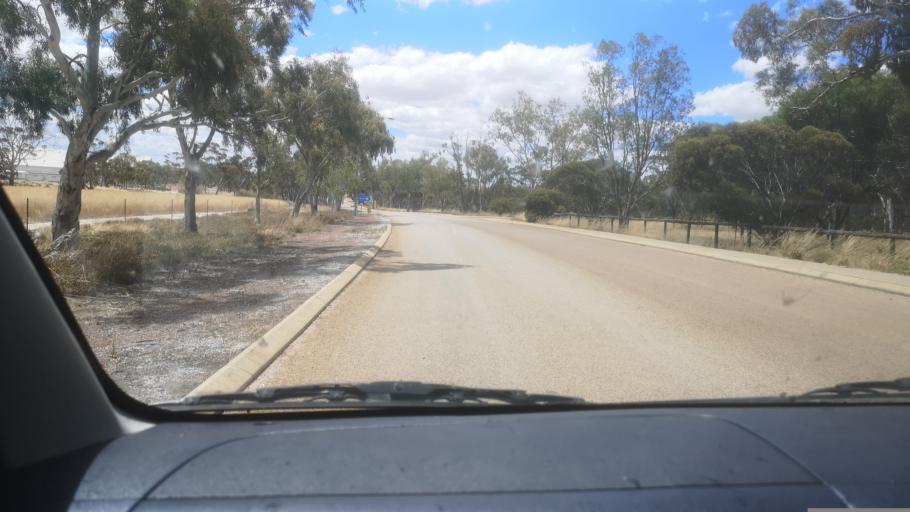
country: AU
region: Western Australia
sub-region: Cunderdin
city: Cunderdin
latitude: -32.0168
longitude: 117.3975
